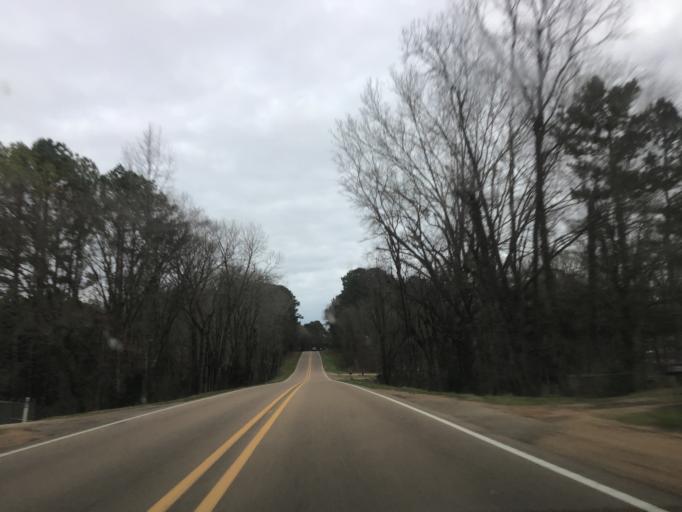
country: US
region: Mississippi
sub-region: Warren County
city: Beechwood
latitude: 32.2781
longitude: -90.7790
